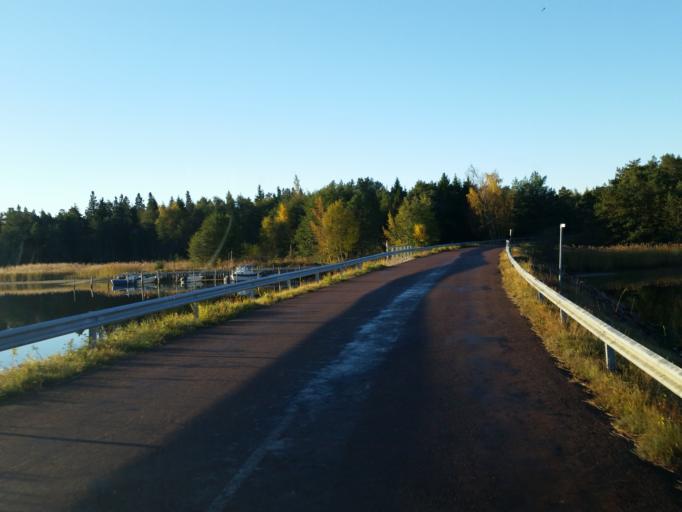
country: AX
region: Alands skaergard
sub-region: Vardoe
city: Vardoe
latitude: 60.2721
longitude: 20.3907
